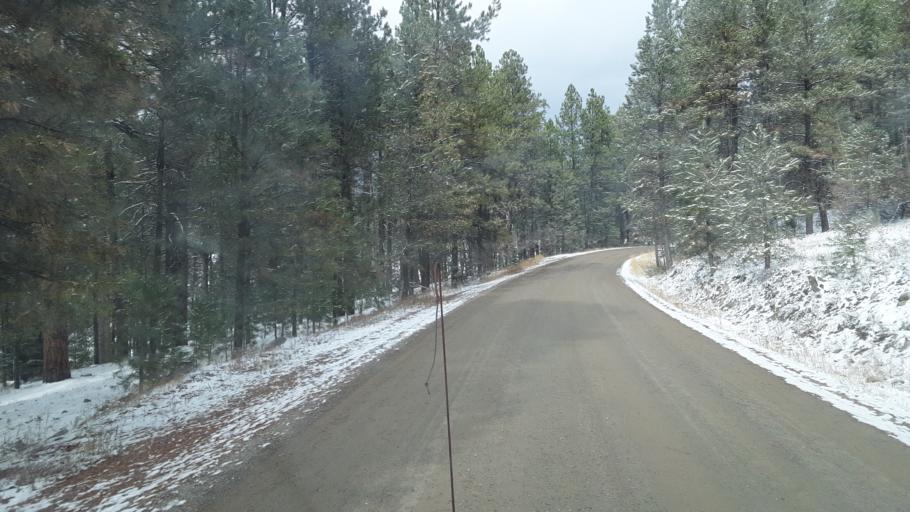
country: US
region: Colorado
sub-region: La Plata County
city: Bayfield
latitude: 37.4105
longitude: -107.5360
